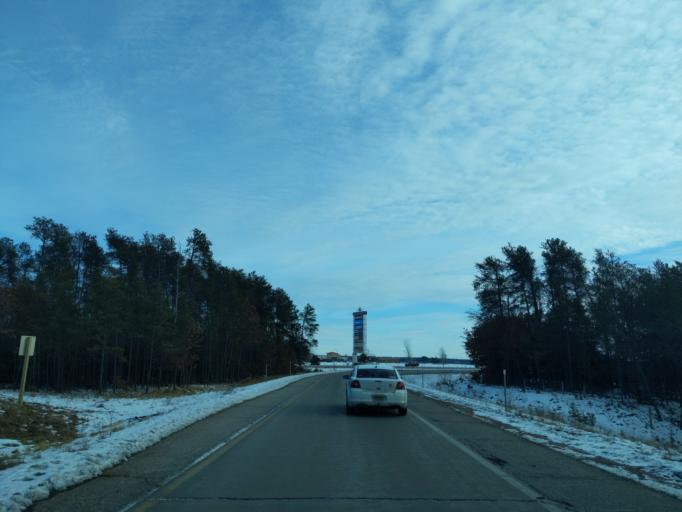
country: US
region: Wisconsin
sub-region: Portage County
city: Whiting
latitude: 44.4949
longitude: -89.5202
